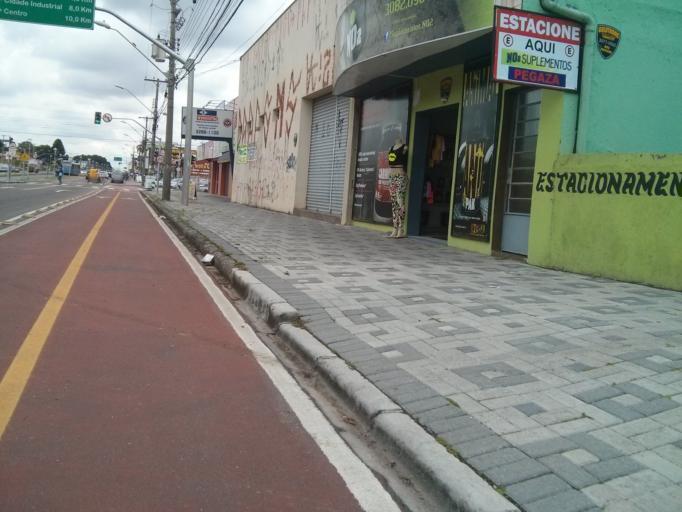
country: BR
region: Parana
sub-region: Sao Jose Dos Pinhais
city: Sao Jose dos Pinhais
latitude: -25.5165
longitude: -49.2301
